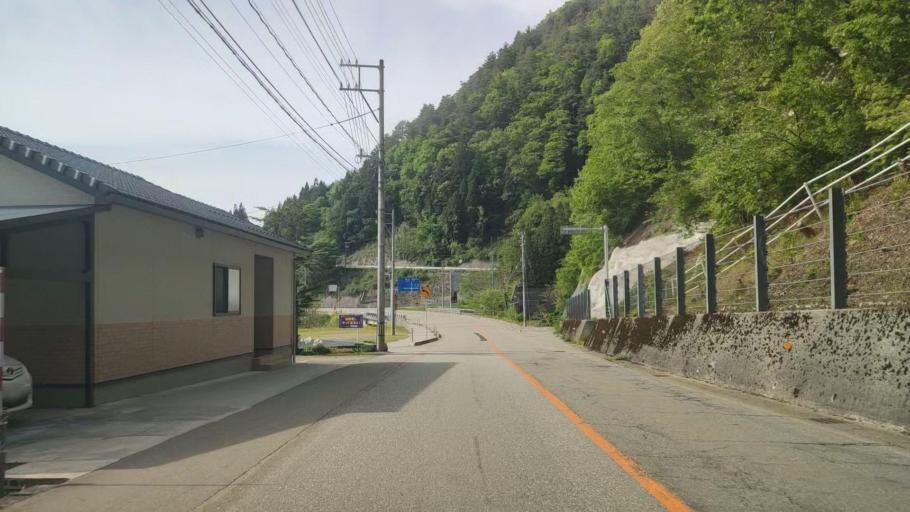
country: JP
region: Gifu
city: Takayama
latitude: 36.3181
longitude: 137.3140
